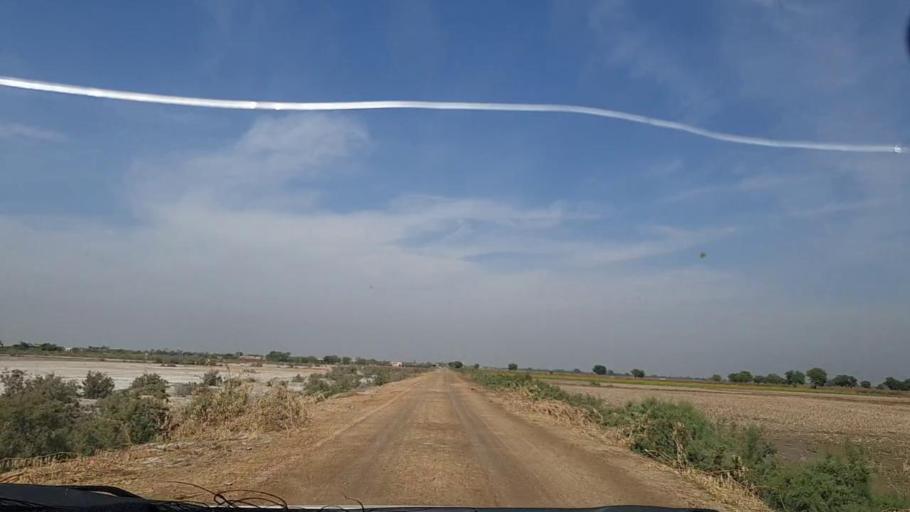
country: PK
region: Sindh
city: Pithoro
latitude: 25.4841
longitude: 69.4564
